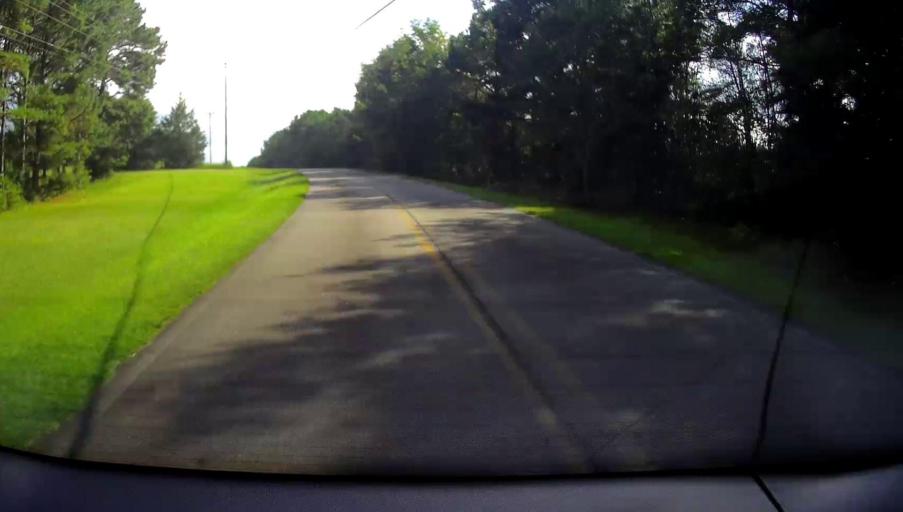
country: US
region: Georgia
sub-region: Upson County
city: Thomaston
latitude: 32.8855
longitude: -84.3523
